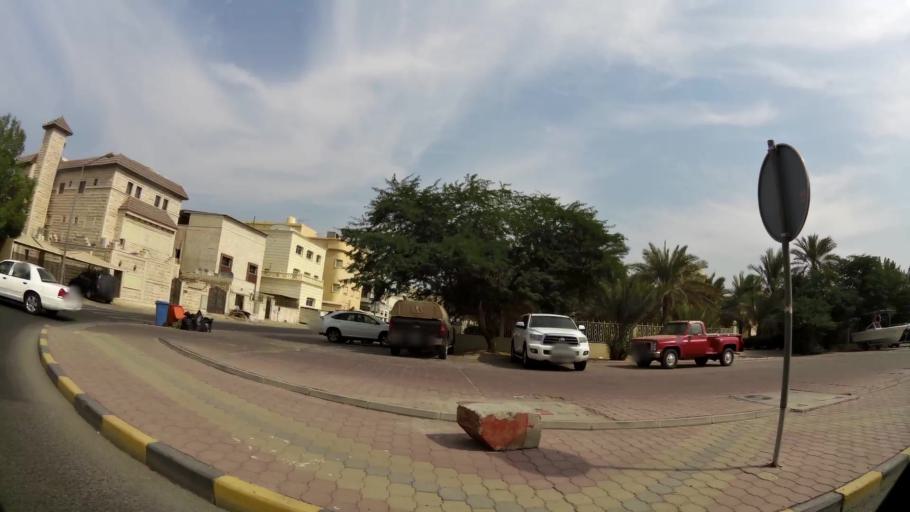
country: KW
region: Al Asimah
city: Ash Shamiyah
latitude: 29.3335
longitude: 47.9773
